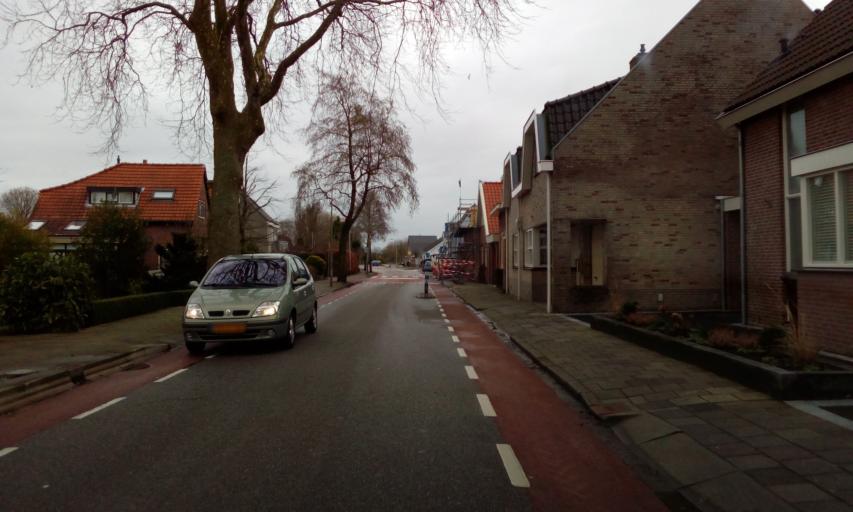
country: NL
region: South Holland
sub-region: Gemeente Alphen aan den Rijn
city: Alphen aan den Rijn
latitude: 52.1303
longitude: 4.6070
